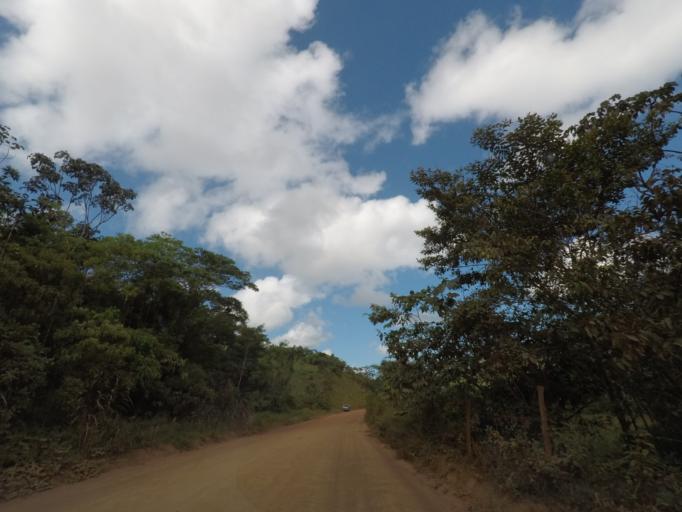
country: BR
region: Bahia
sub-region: Itacare
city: Itacare
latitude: -14.2210
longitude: -39.0758
